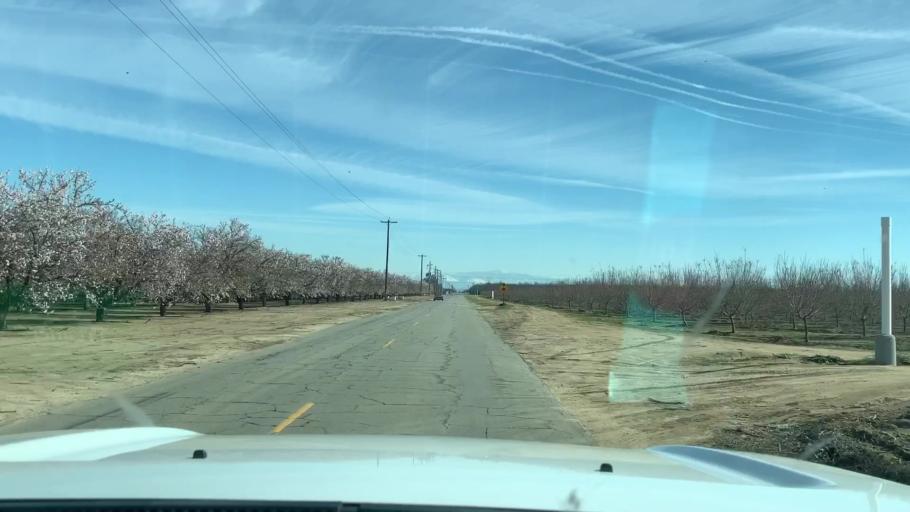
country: US
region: California
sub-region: Kern County
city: Shafter
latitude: 35.4853
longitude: -119.2652
